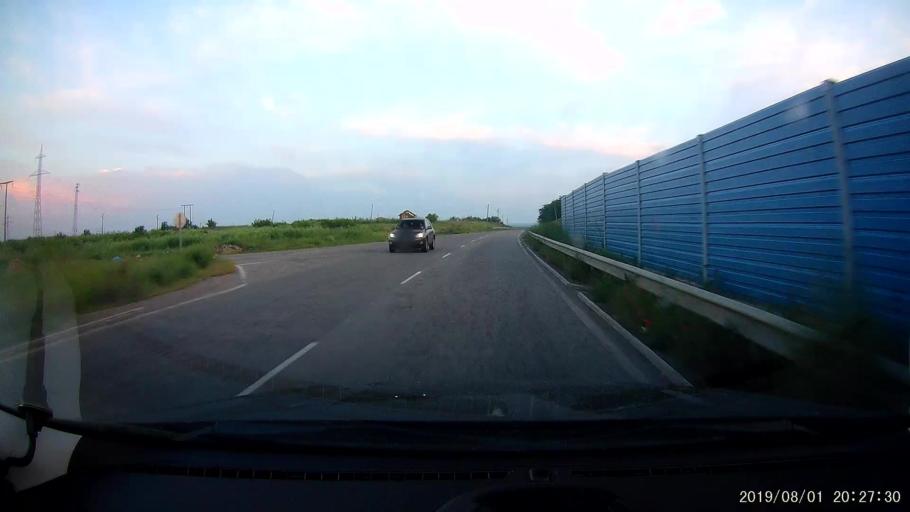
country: BG
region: Yambol
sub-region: Obshtina Elkhovo
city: Elkhovo
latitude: 42.1793
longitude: 26.5845
